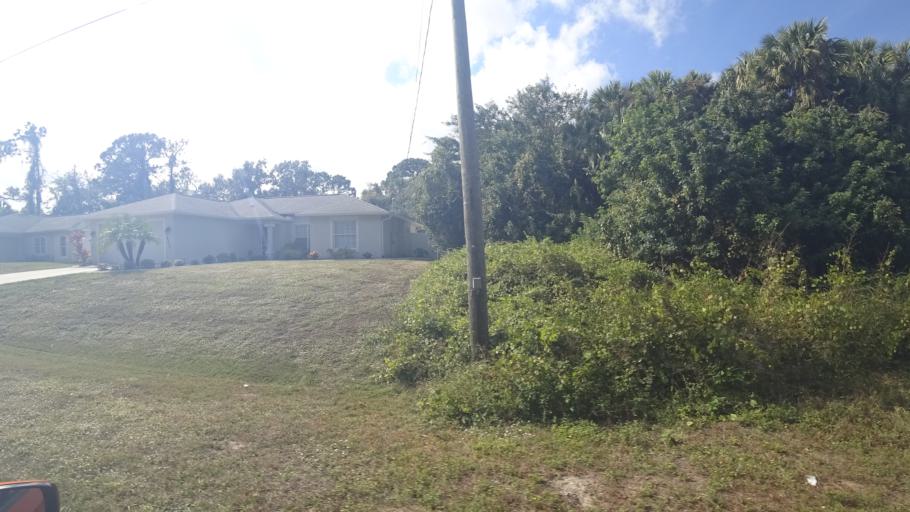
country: US
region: Florida
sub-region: Charlotte County
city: Port Charlotte
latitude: 27.0469
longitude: -82.1296
